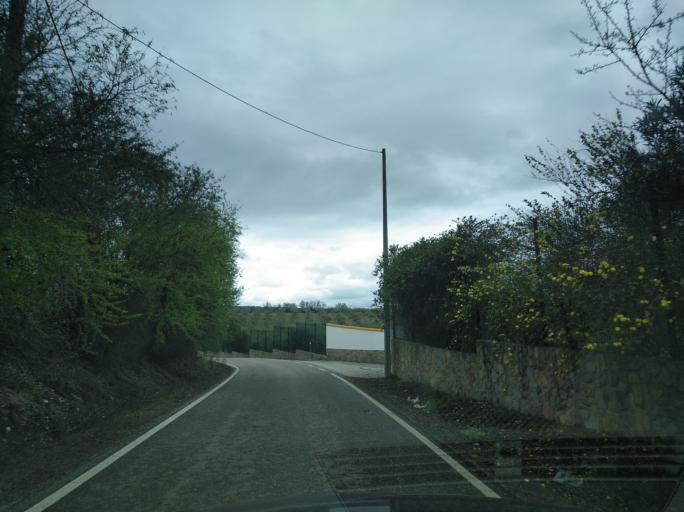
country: PT
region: Portalegre
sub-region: Campo Maior
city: Campo Maior
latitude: 38.9918
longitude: -7.0482
